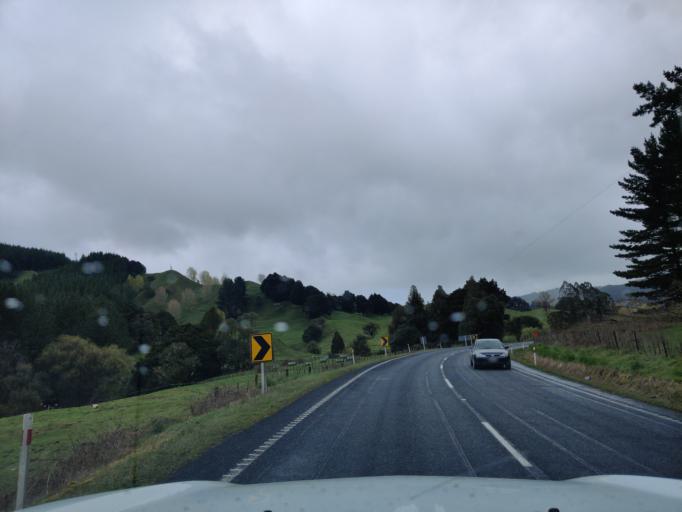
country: NZ
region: Waikato
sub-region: Otorohanga District
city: Otorohanga
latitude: -38.6640
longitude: 175.2068
